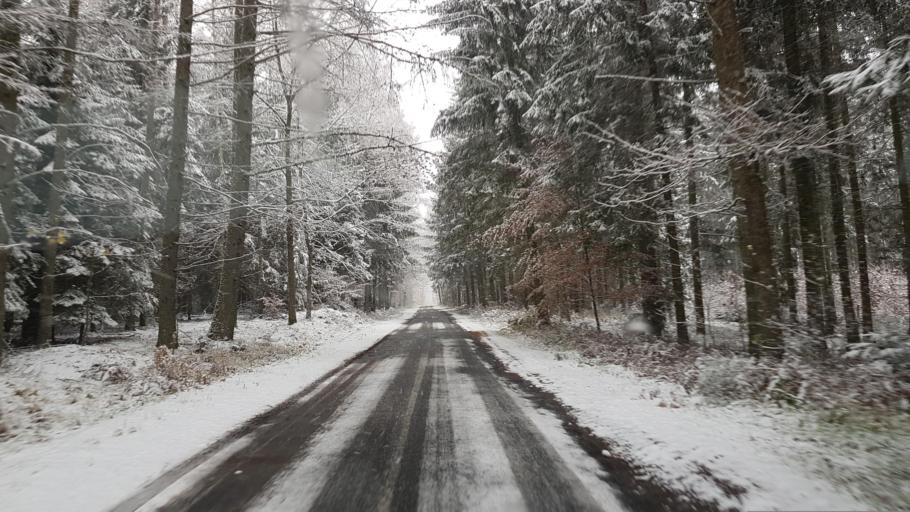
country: PL
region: West Pomeranian Voivodeship
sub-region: Powiat lobeski
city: Resko
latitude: 53.7966
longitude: 15.5336
